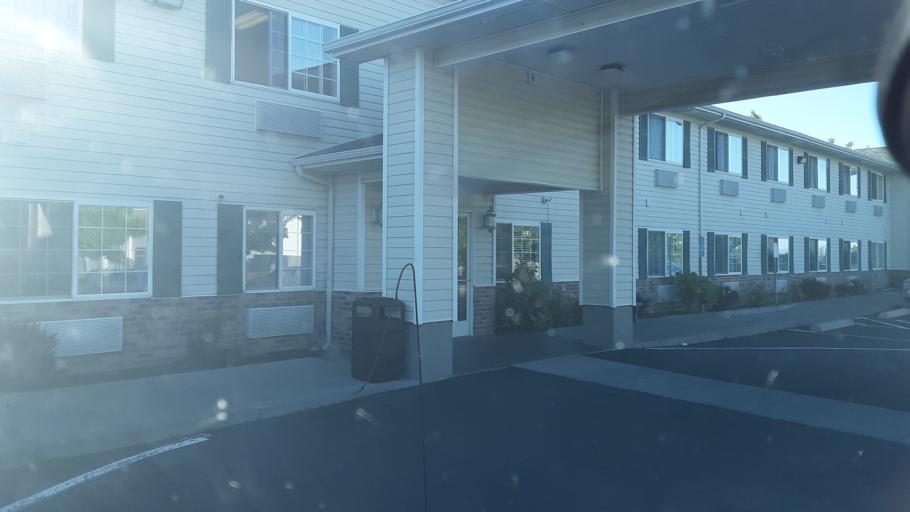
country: US
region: Oregon
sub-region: Deschutes County
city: Bend
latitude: 44.1154
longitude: -121.2931
